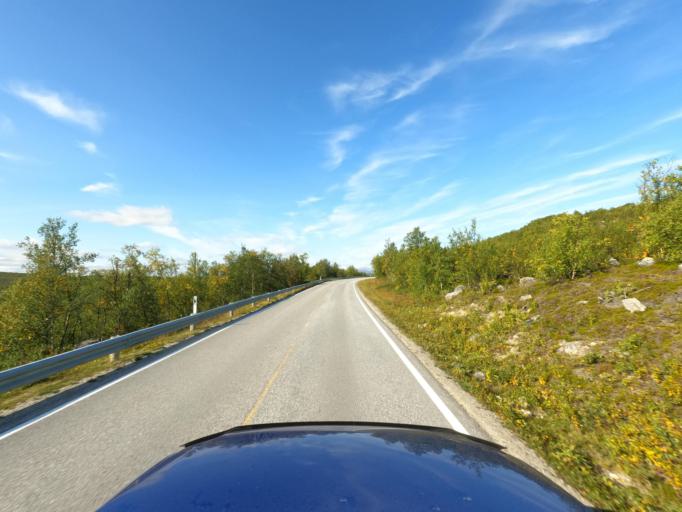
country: NO
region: Finnmark Fylke
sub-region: Porsanger
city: Lakselv
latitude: 69.7675
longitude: 25.1719
